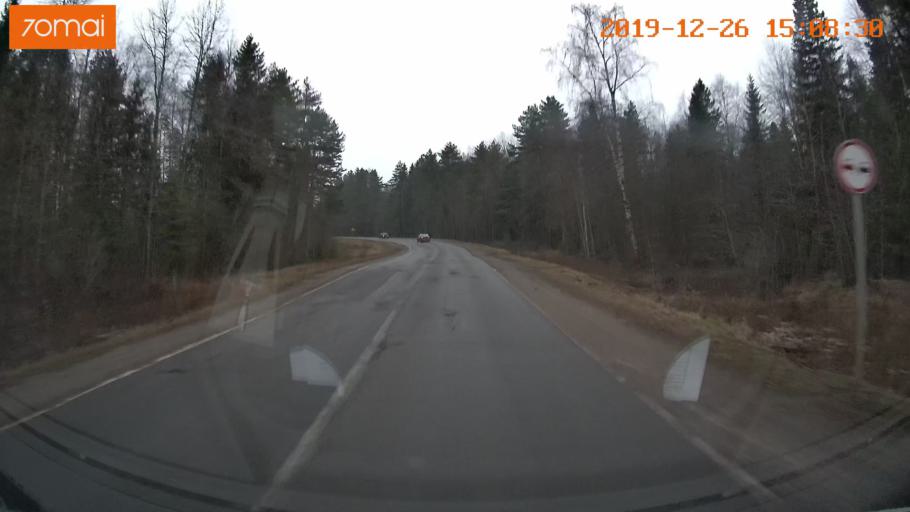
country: RU
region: Jaroslavl
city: Rybinsk
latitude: 58.1591
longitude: 38.8376
